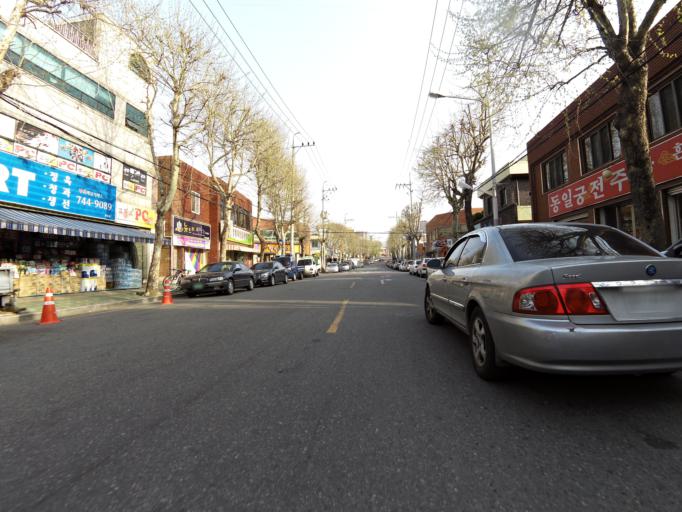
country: KR
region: Daegu
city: Daegu
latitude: 35.8656
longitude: 128.6432
